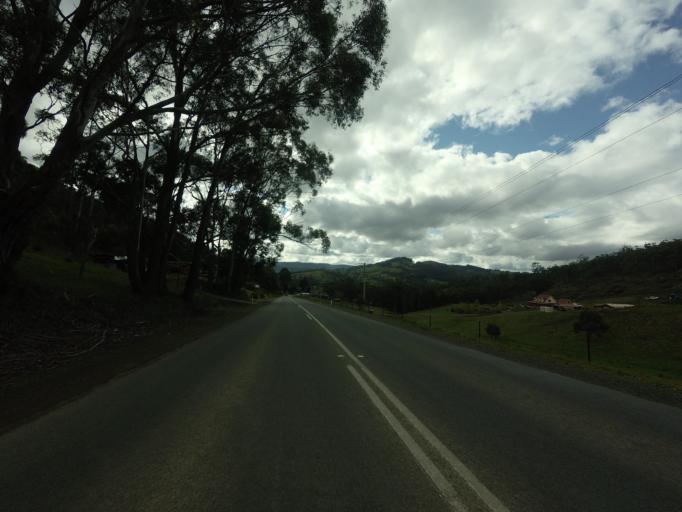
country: AU
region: Tasmania
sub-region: Huon Valley
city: Geeveston
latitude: -43.1798
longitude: 146.9510
